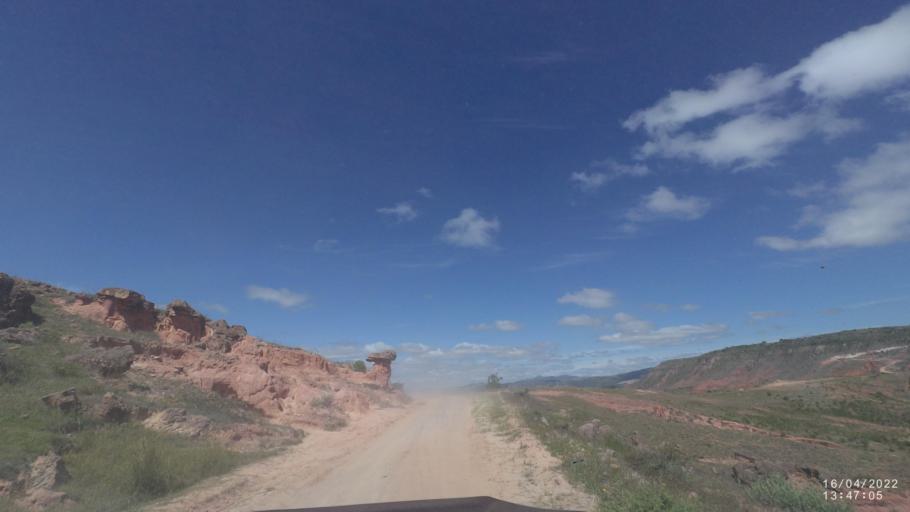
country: BO
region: Cochabamba
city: Mizque
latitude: -18.0067
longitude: -65.5851
